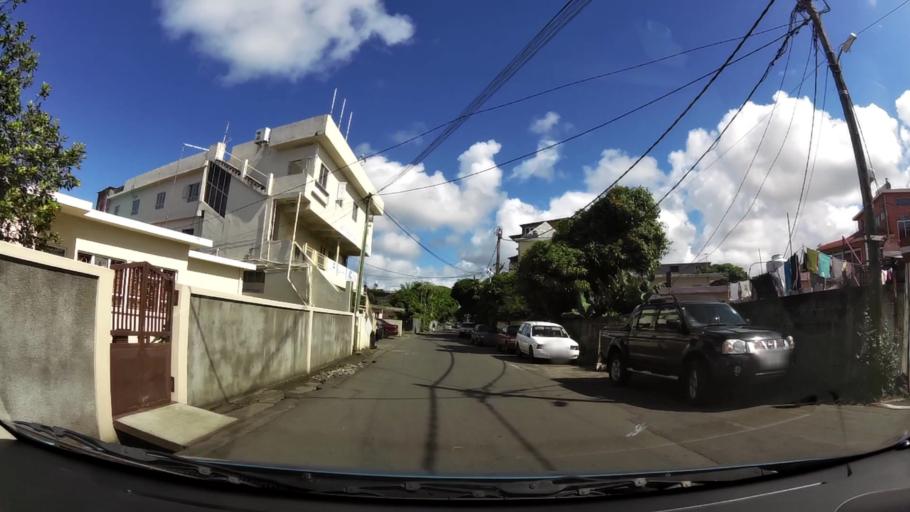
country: MU
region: Grand Port
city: Plaine Magnien
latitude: -20.4300
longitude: 57.6689
